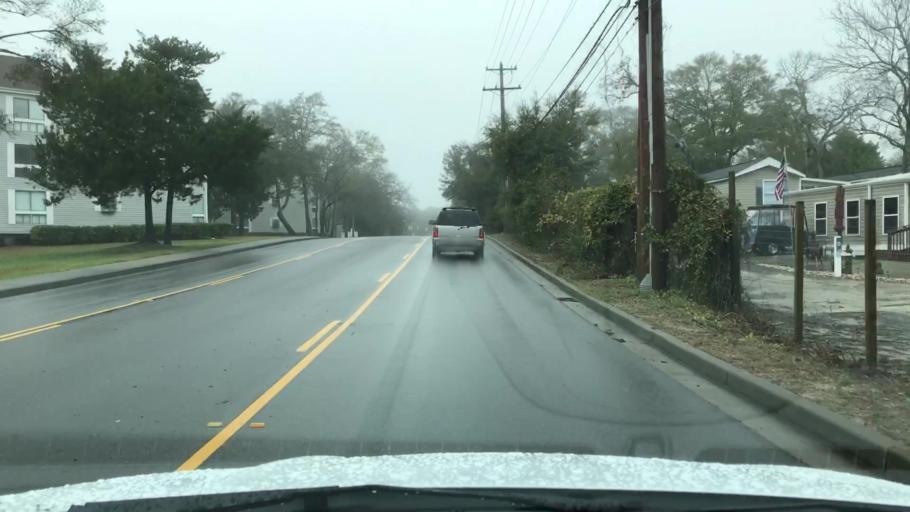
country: US
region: South Carolina
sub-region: Horry County
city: North Myrtle Beach
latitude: 33.7664
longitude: -78.7873
